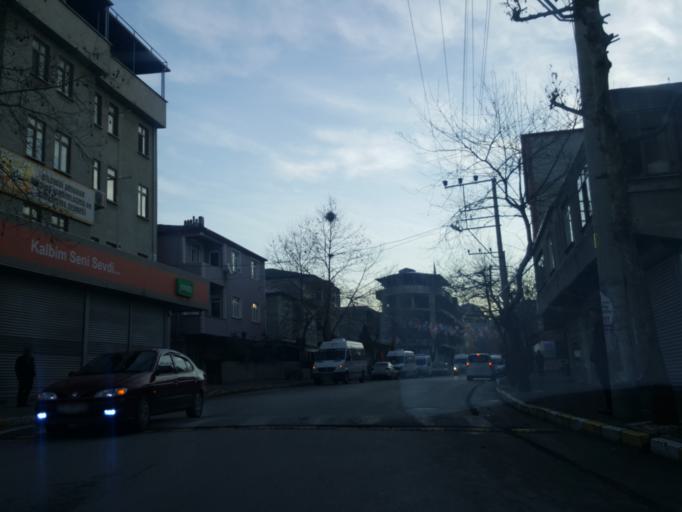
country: TR
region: Kocaeli
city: Tavsancil
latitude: 40.7902
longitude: 29.5407
